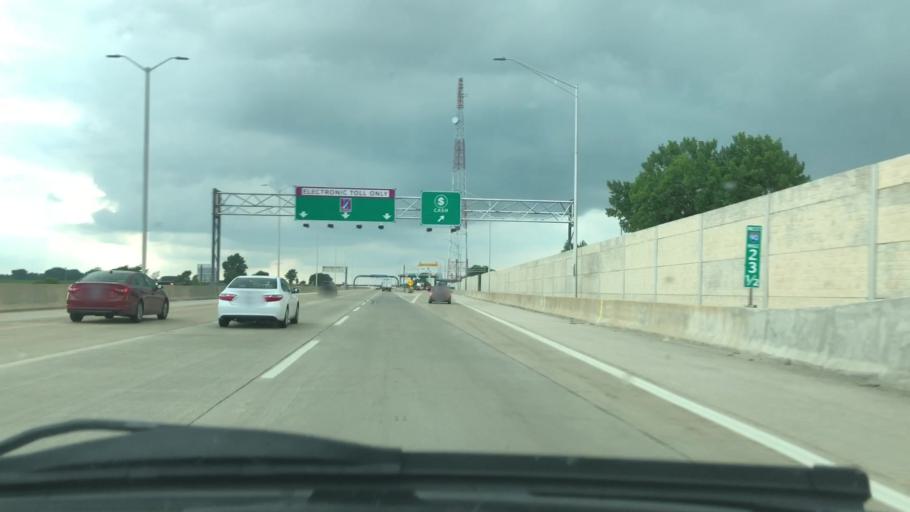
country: US
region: Illinois
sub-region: Boone County
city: Belvidere
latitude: 42.2337
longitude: -88.8482
